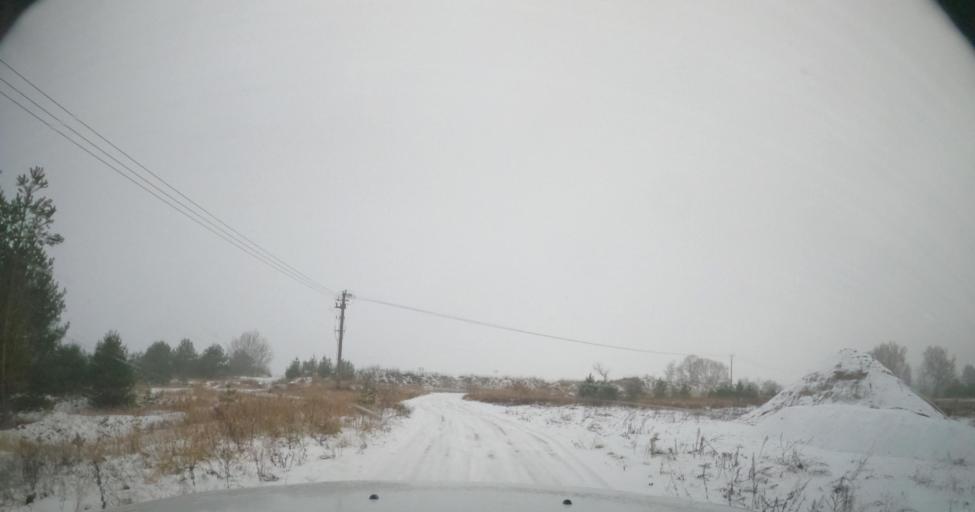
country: PL
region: West Pomeranian Voivodeship
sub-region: Powiat kamienski
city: Golczewo
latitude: 53.7819
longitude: 14.9566
